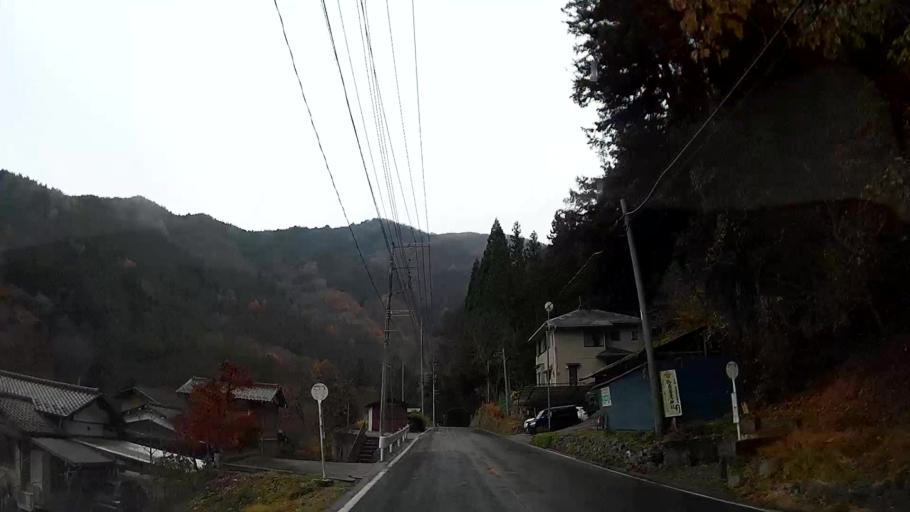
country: JP
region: Saitama
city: Chichibu
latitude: 35.9474
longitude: 138.9321
